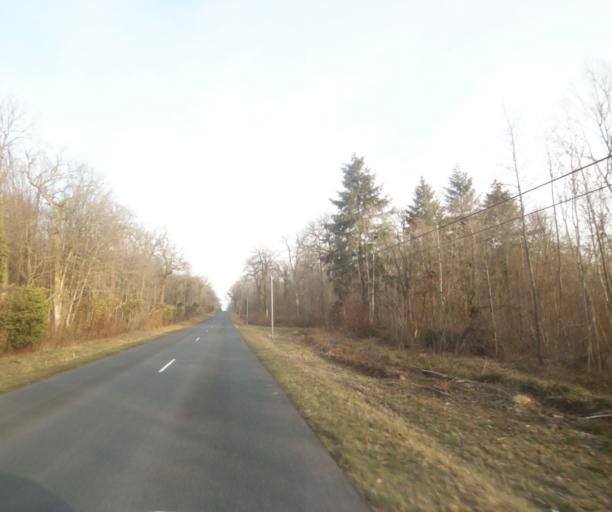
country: FR
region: Champagne-Ardenne
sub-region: Departement de la Haute-Marne
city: Chancenay
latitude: 48.6959
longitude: 4.9454
